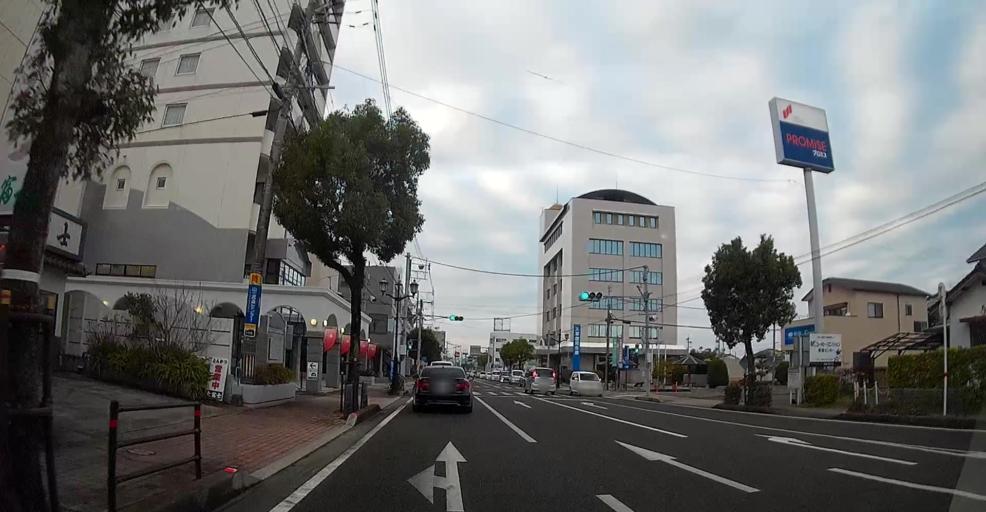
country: JP
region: Kumamoto
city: Hondo
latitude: 32.4507
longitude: 130.1979
